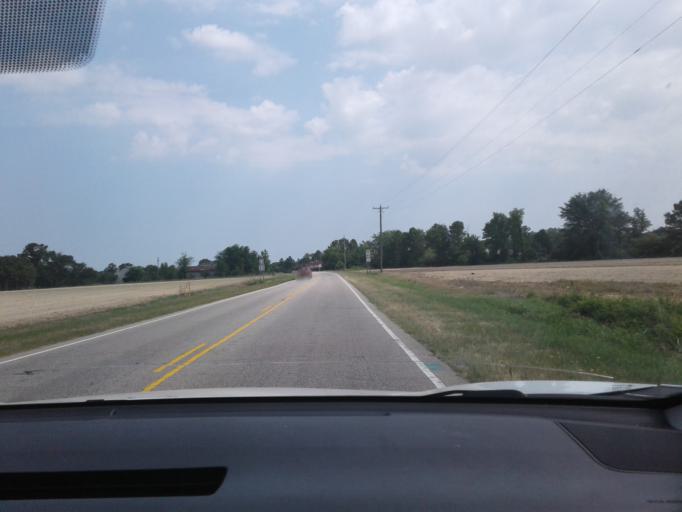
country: US
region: North Carolina
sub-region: Harnett County
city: Coats
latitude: 35.3694
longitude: -78.6618
